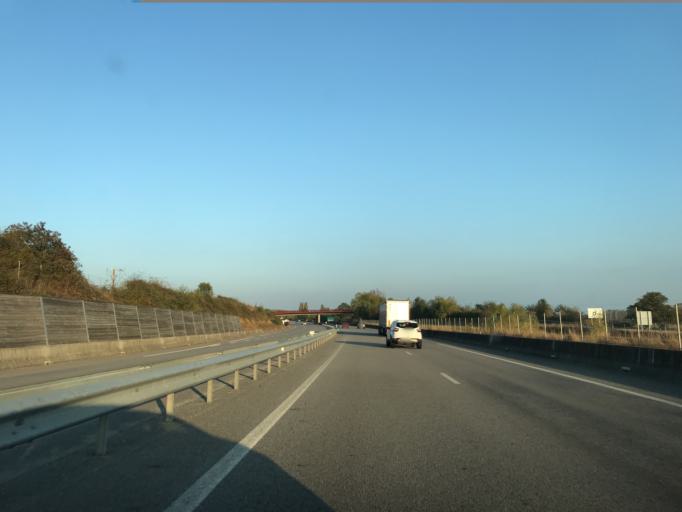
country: FR
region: Lower Normandy
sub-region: Departement de l'Orne
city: Valframbert
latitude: 48.4745
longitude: 0.1975
